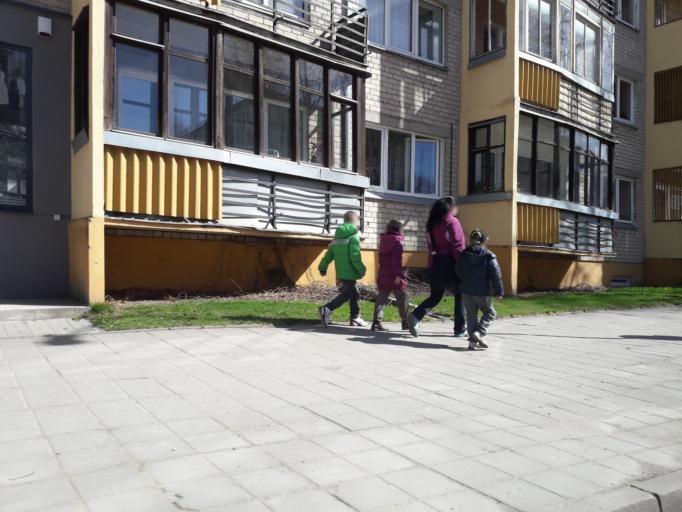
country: LT
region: Siauliu apskritis
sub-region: Siauliai
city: Siauliai
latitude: 55.9365
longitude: 23.3115
